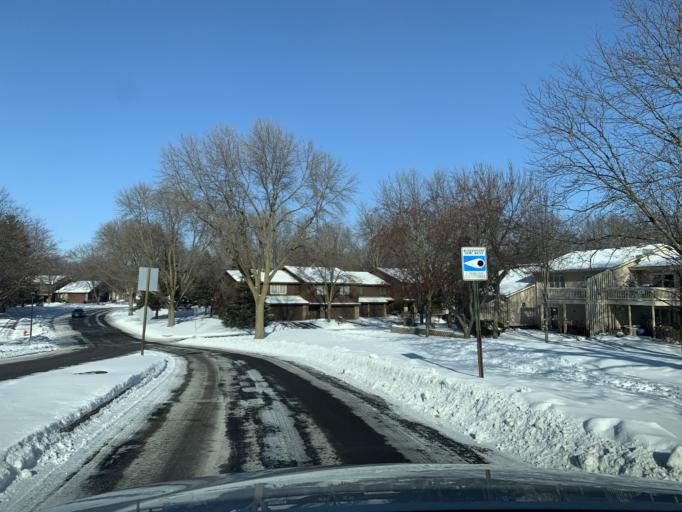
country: US
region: Minnesota
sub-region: Hennepin County
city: Edina
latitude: 44.8334
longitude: -93.3583
